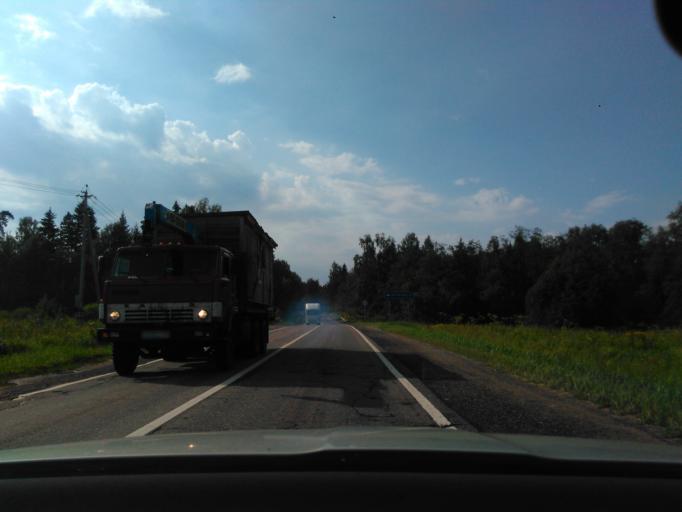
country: RU
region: Moskovskaya
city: Solnechnogorsk
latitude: 56.1415
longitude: 36.8365
